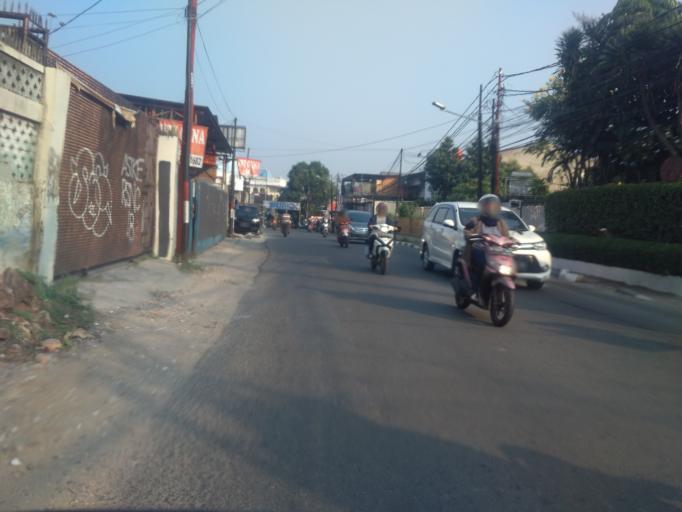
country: ID
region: Jakarta Raya
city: Jakarta
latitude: -6.2638
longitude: 106.7953
